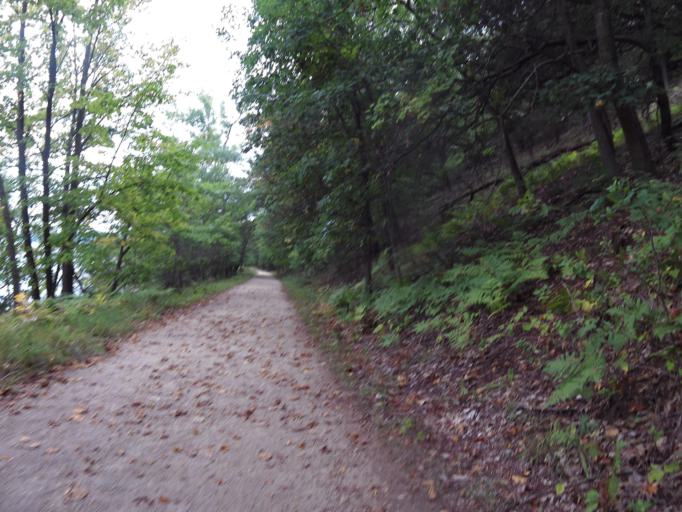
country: US
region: Minnesota
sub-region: Washington County
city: Afton
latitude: 44.8685
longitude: -92.7708
